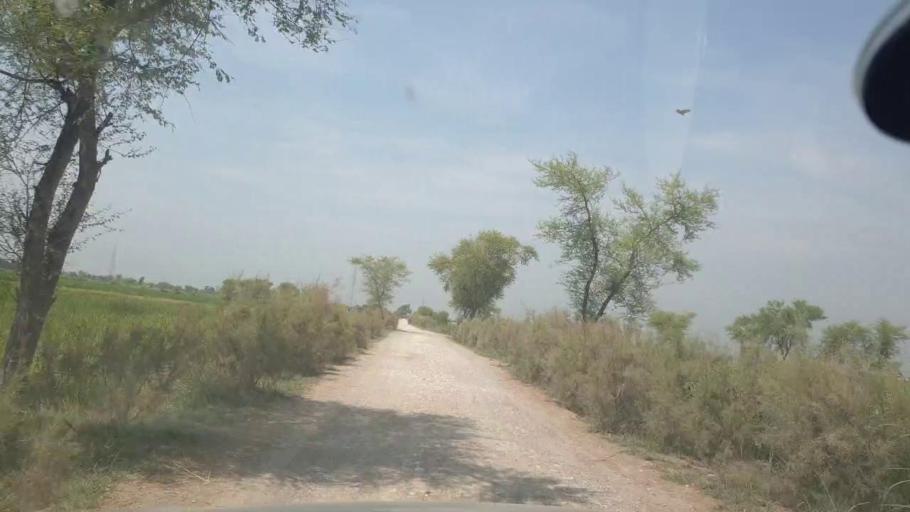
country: PK
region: Sindh
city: Thul
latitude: 28.1785
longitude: 68.6201
